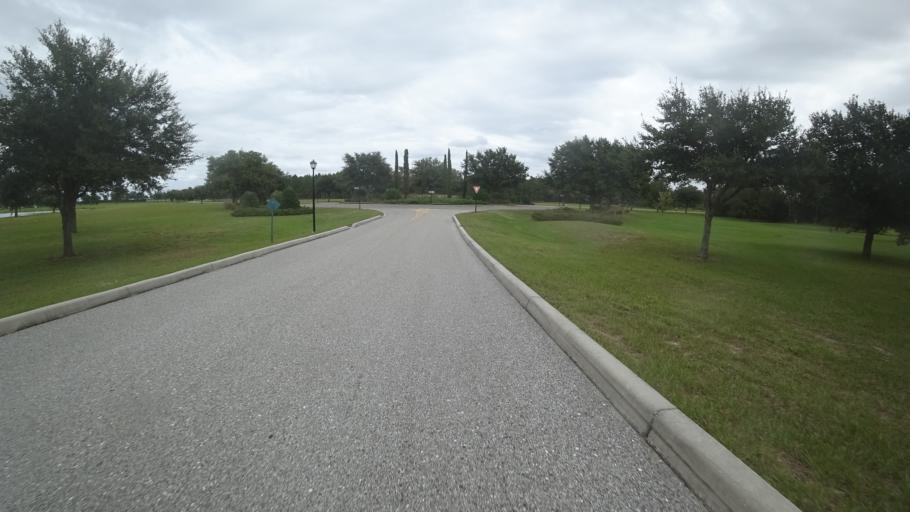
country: US
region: Florida
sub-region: Hillsborough County
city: Wimauma
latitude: 27.6541
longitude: -82.3262
